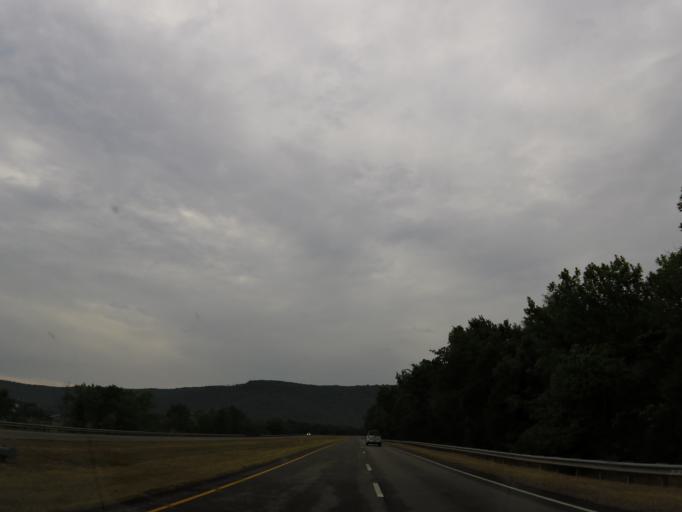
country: US
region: Alabama
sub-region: Madison County
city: New Hope
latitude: 34.6251
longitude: -86.3077
